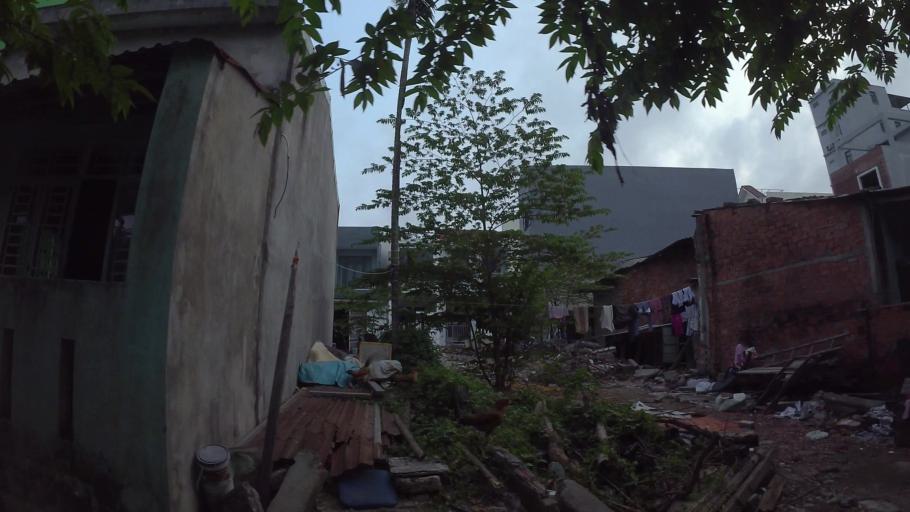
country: VN
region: Da Nang
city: Son Tra
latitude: 16.0608
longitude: 108.2335
